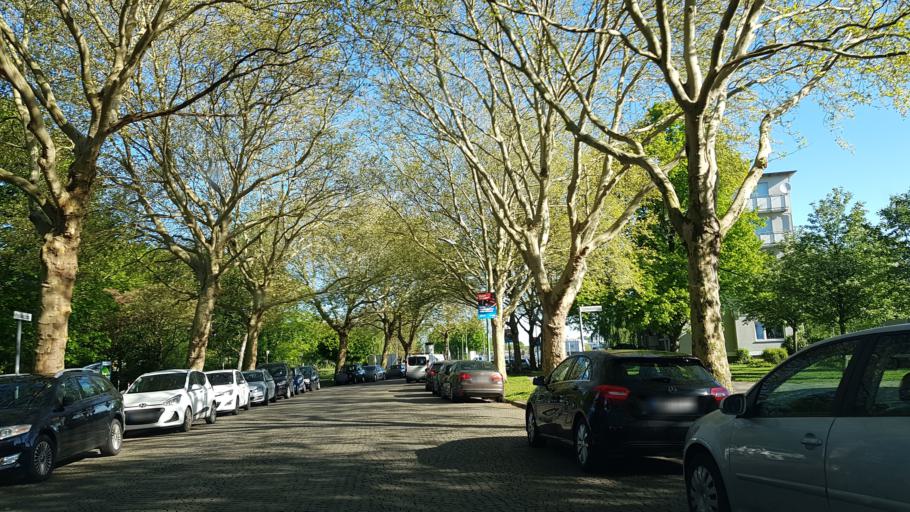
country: DE
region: Bremen
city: Bremerhaven
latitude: 53.5591
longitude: 8.5732
